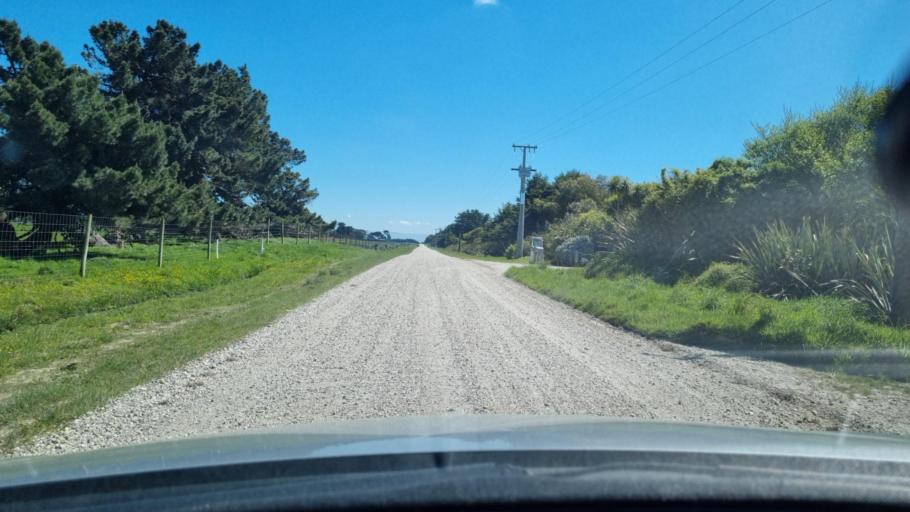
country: NZ
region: Southland
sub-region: Invercargill City
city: Invercargill
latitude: -46.4218
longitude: 168.2756
